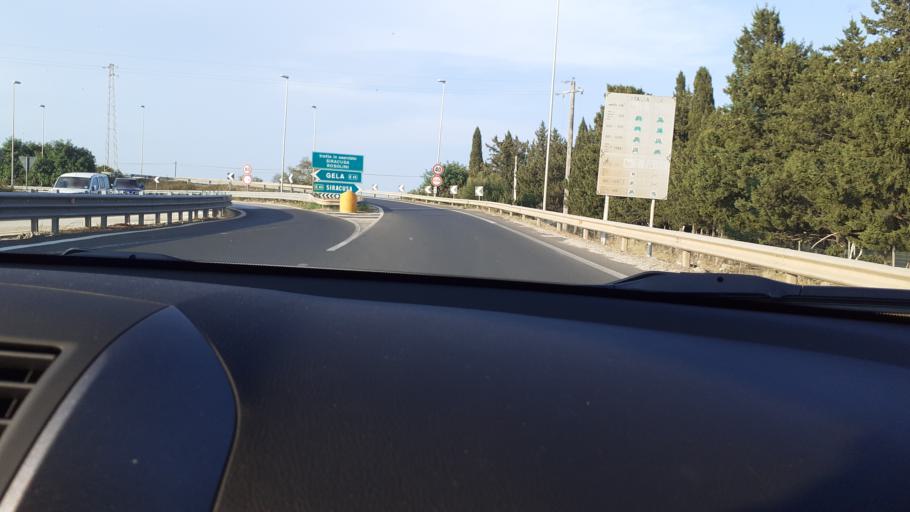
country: IT
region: Sicily
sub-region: Provincia di Siracusa
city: Cassibile
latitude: 36.9730
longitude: 15.1915
